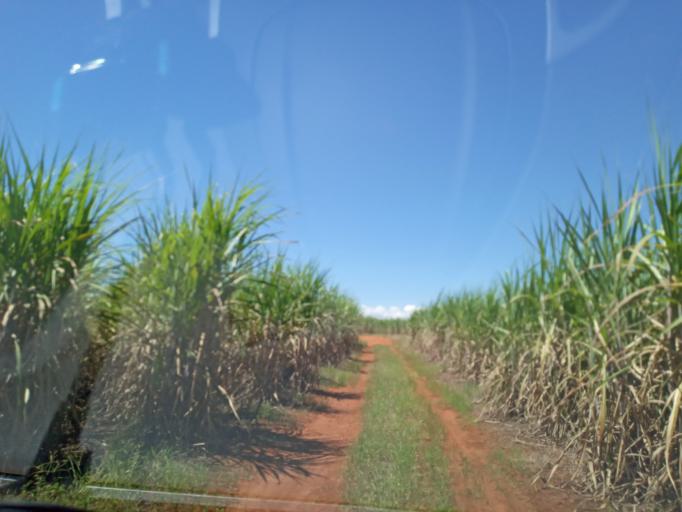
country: BR
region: Goias
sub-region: Itumbiara
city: Itumbiara
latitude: -18.4001
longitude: -49.1214
